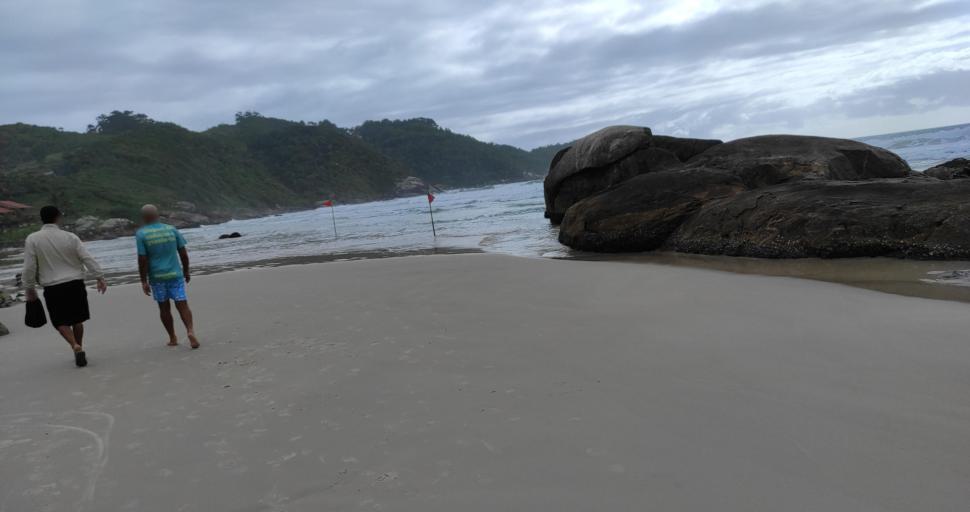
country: BR
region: Santa Catarina
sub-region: Porto Belo
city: Porto Belo
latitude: -27.1674
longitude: -48.4973
